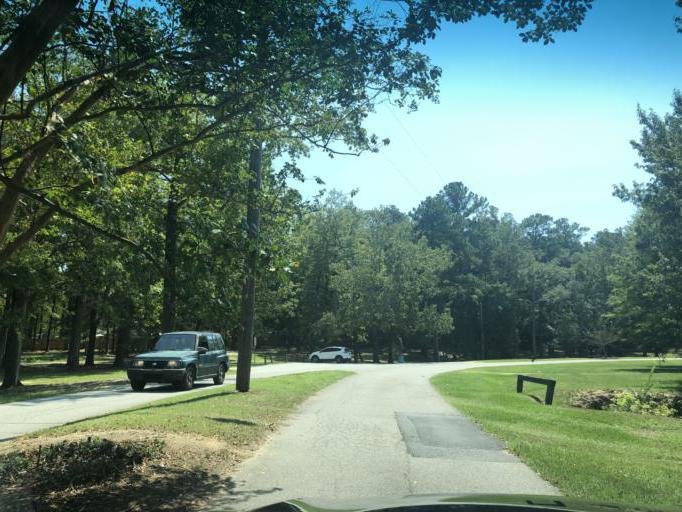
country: US
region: Georgia
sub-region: Muscogee County
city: Columbus
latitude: 32.5098
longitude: -84.9083
